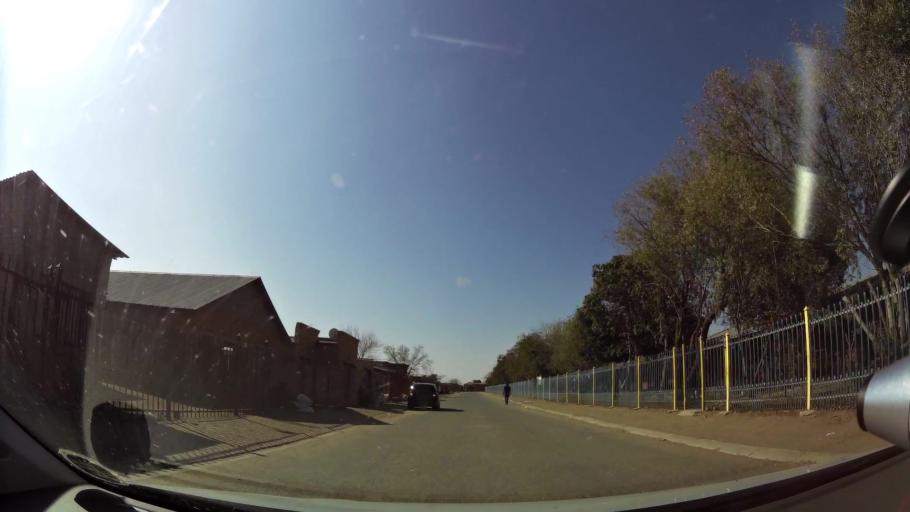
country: ZA
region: Orange Free State
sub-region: Mangaung Metropolitan Municipality
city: Bloemfontein
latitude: -29.1483
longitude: 26.2412
